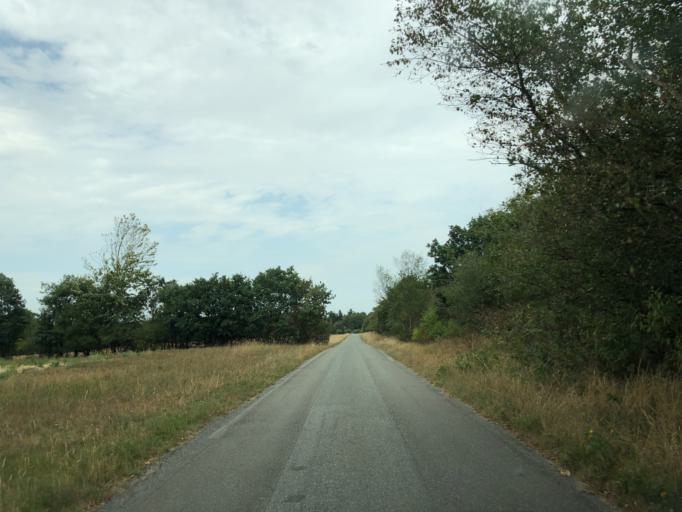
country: DK
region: Central Jutland
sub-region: Holstebro Kommune
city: Ulfborg
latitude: 56.2256
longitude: 8.3254
